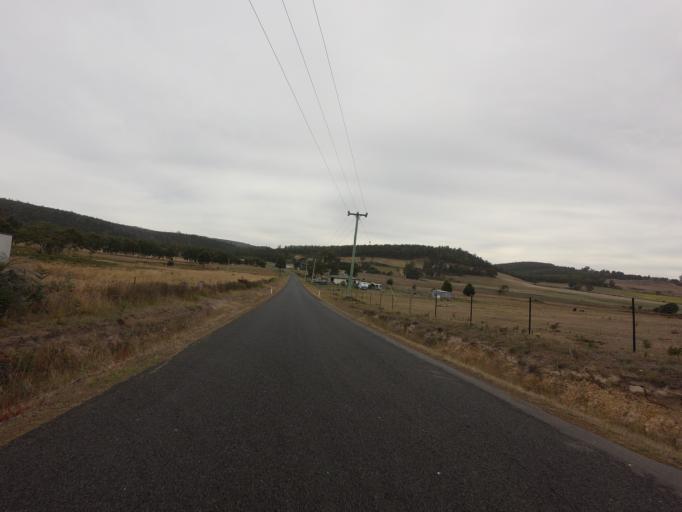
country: AU
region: Tasmania
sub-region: Sorell
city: Sorell
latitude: -42.5655
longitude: 147.5720
